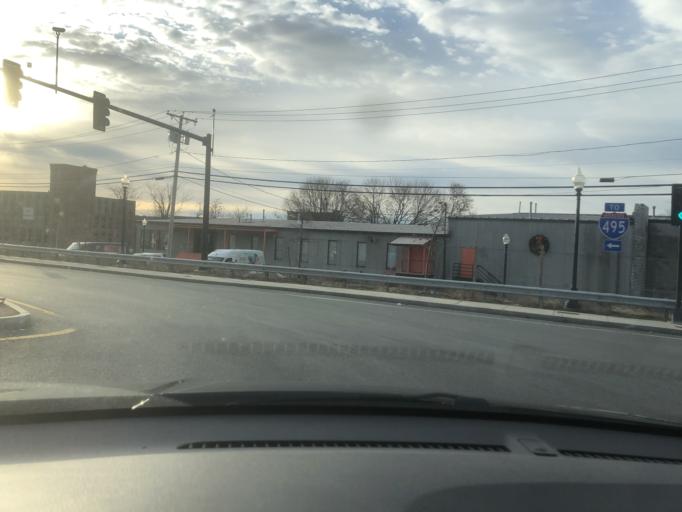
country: US
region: Massachusetts
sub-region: Essex County
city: North Andover
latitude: 42.7078
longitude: -71.1474
